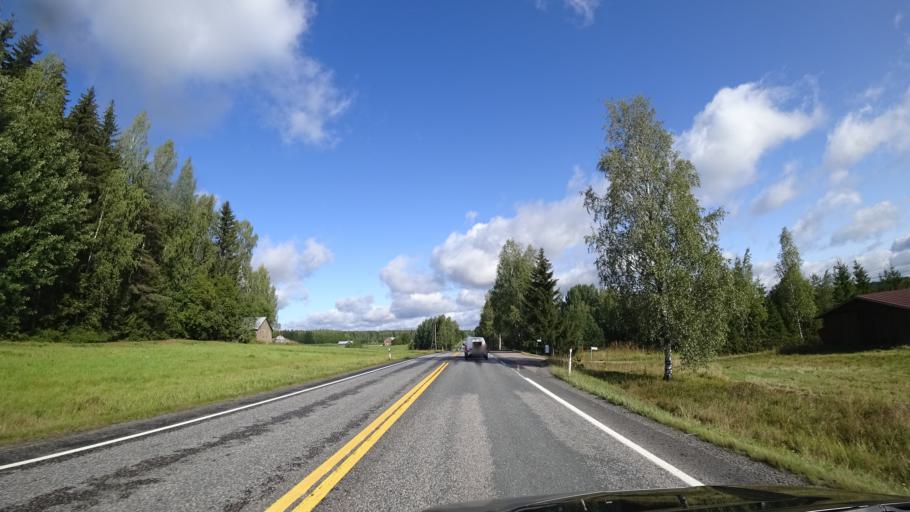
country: FI
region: Uusimaa
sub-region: Helsinki
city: Tuusula
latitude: 60.4606
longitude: 24.9479
